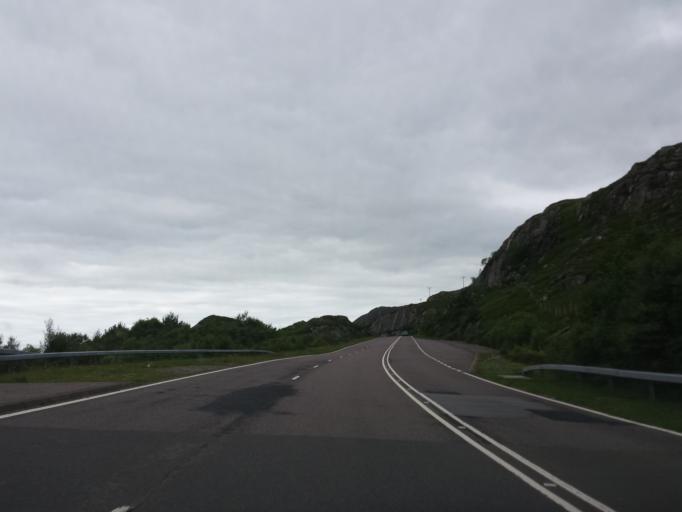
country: GB
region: Scotland
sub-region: Argyll and Bute
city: Isle Of Mull
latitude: 56.8833
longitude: -5.6983
